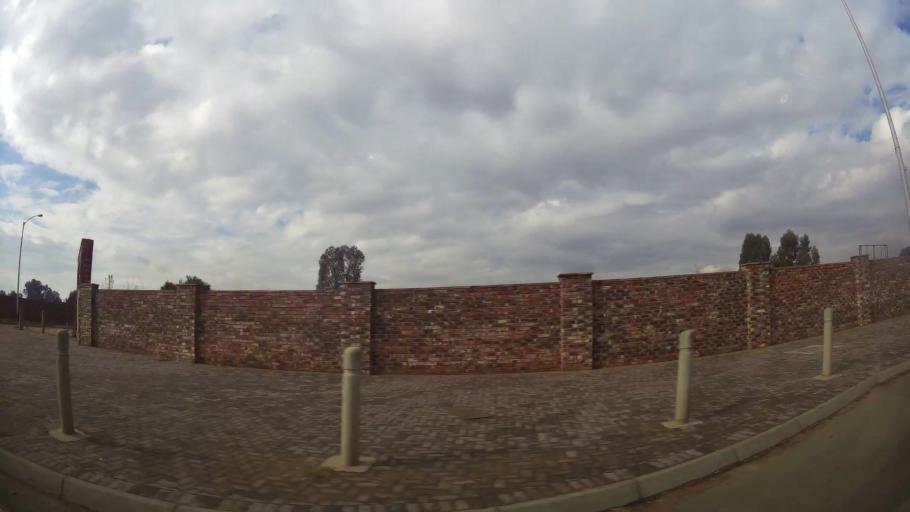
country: ZA
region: Gauteng
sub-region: Sedibeng District Municipality
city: Meyerton
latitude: -26.5883
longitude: 28.0041
